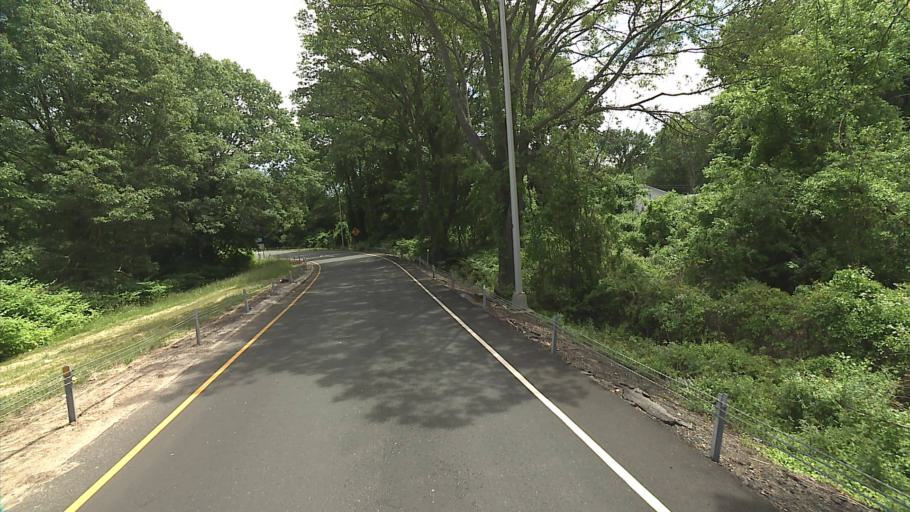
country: US
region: Connecticut
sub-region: New London County
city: Central Waterford
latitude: 41.3698
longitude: -72.1340
